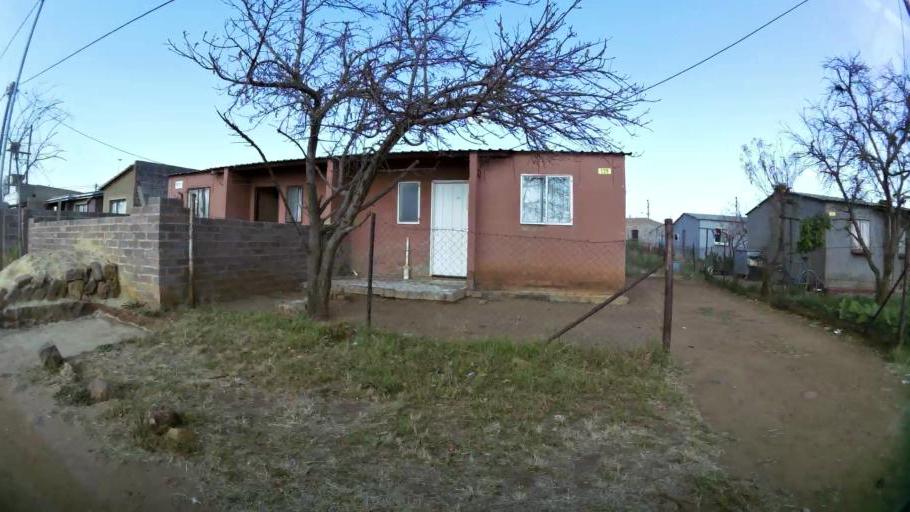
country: ZA
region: Gauteng
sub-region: City of Johannesburg Metropolitan Municipality
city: Soweto
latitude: -26.2550
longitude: 27.8948
